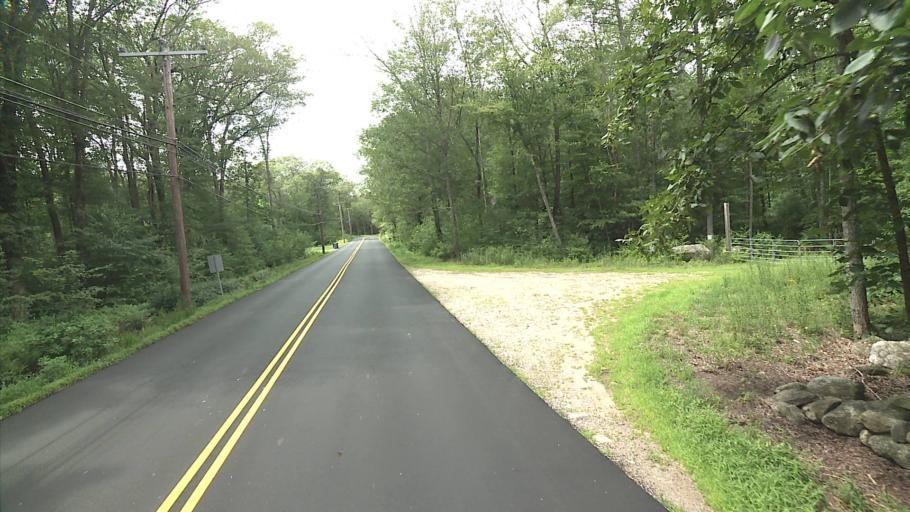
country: US
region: Connecticut
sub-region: Windham County
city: South Woodstock
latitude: 41.9391
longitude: -71.9980
